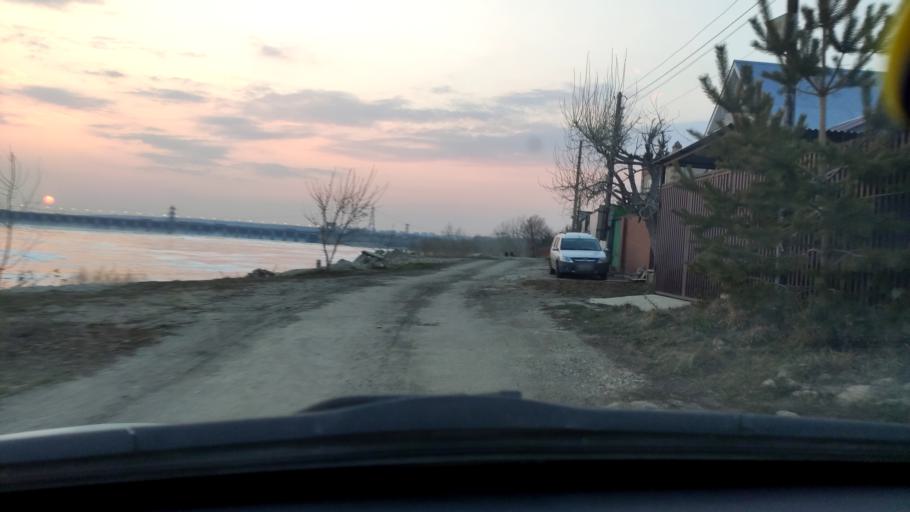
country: RU
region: Samara
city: Zhigulevsk
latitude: 53.4527
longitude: 49.5207
